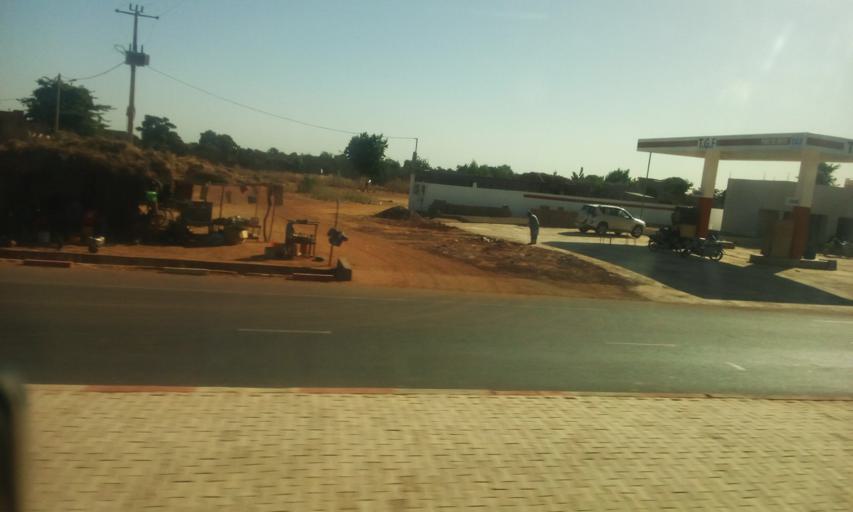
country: ML
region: Segou
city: Segou
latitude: 13.4146
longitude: -6.3197
